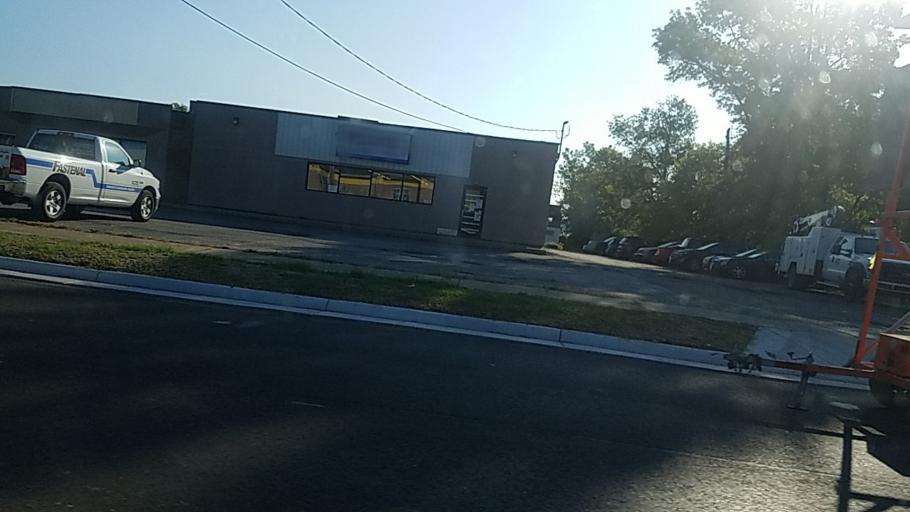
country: US
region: Ohio
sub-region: Trumbull County
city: Girard
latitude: 41.1260
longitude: -80.7111
